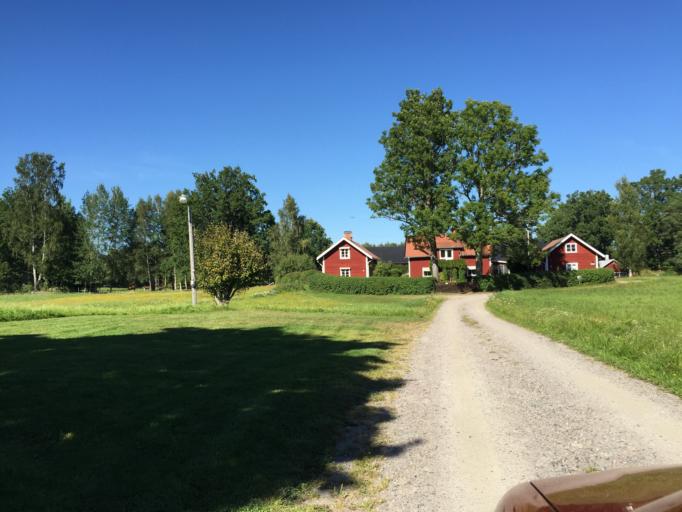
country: SE
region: OErebro
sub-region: Hallsbergs Kommun
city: Palsboda
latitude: 58.8849
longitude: 15.5513
